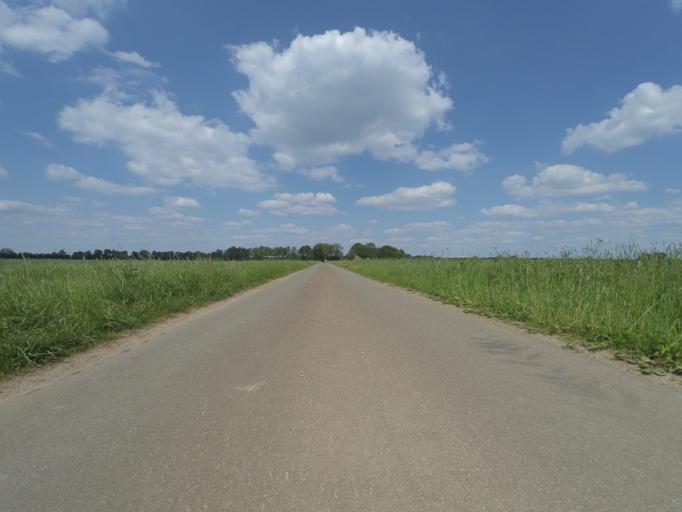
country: DE
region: Lower Saxony
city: Haenigsen
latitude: 52.5112
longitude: 10.0716
